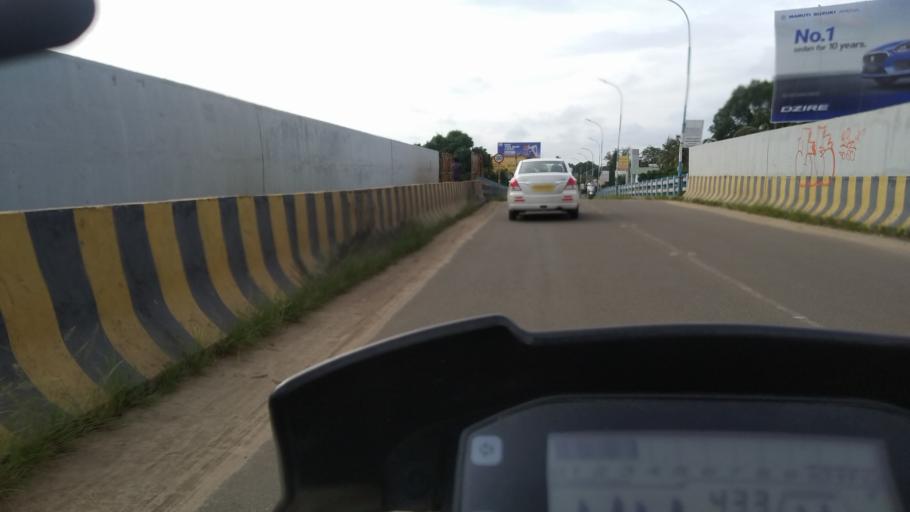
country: IN
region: Kerala
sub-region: Ernakulam
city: Cochin
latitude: 9.9759
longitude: 76.3149
